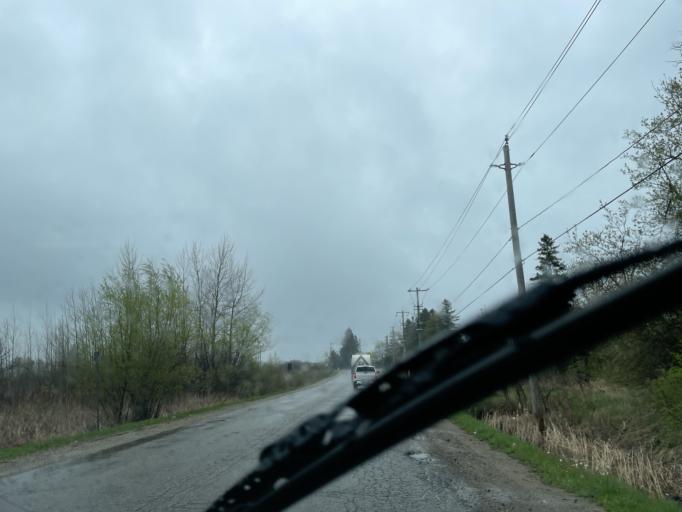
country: CA
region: Ontario
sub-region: Wellington County
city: Guelph
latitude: 43.5526
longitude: -80.3018
